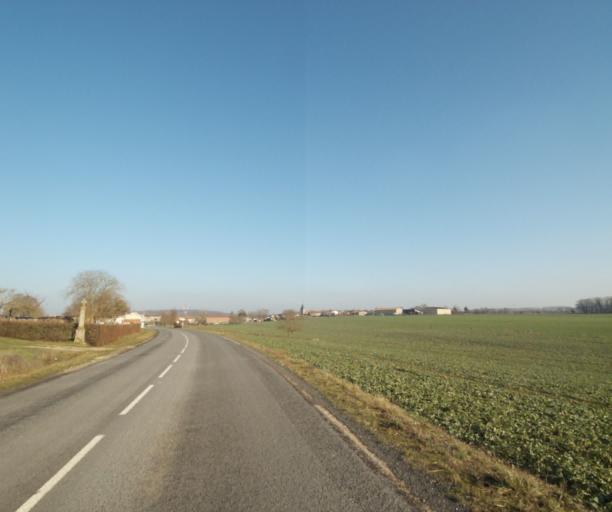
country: FR
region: Champagne-Ardenne
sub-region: Departement de la Haute-Marne
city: Wassy
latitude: 48.5106
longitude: 4.9975
